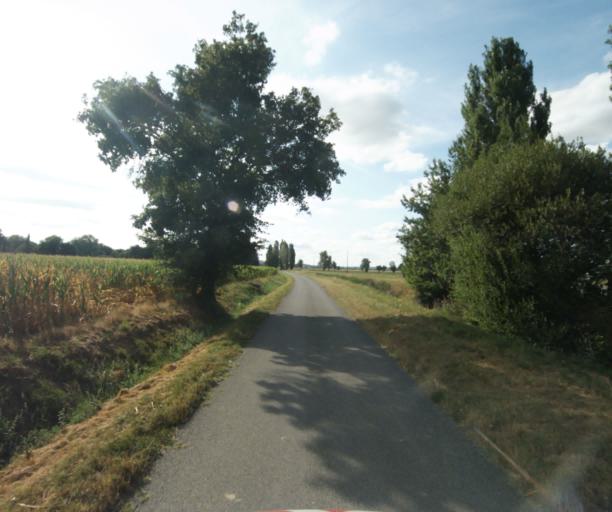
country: FR
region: Midi-Pyrenees
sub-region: Departement de la Haute-Garonne
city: Revel
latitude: 43.5052
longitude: 1.9919
